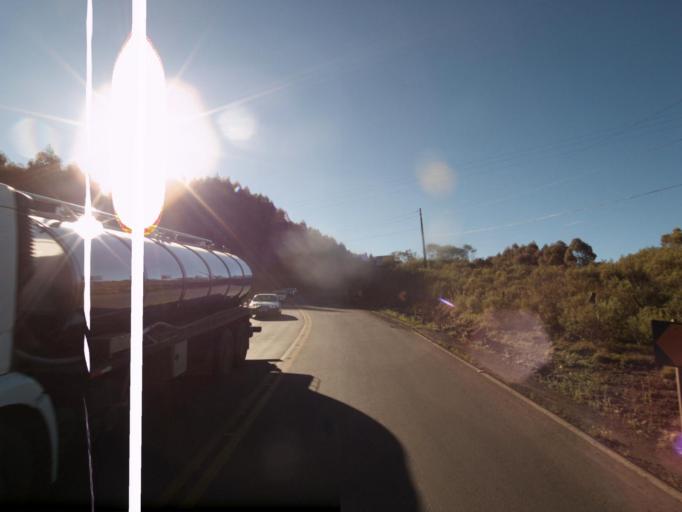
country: AR
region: Misiones
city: Bernardo de Irigoyen
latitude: -26.4754
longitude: -53.5069
